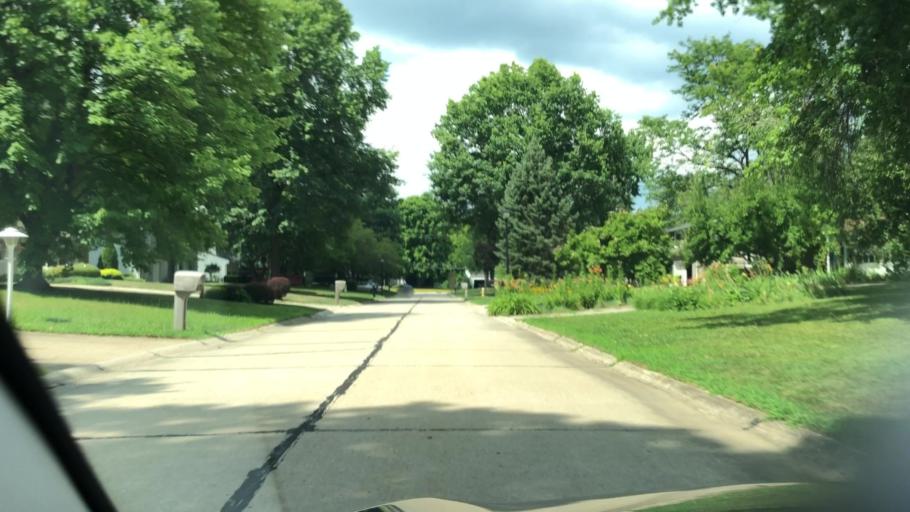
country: US
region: Ohio
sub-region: Summit County
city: Fairlawn
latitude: 41.1247
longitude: -81.6293
